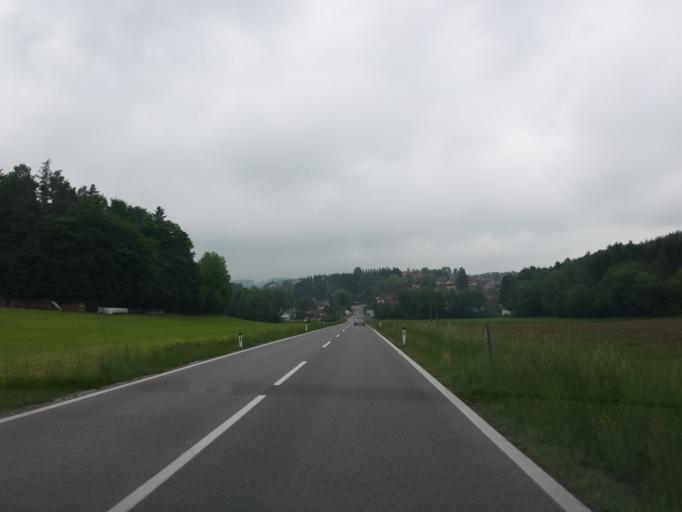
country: AT
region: Styria
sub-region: Politischer Bezirk Graz-Umgebung
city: Kumberg
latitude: 47.1466
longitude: 15.5485
